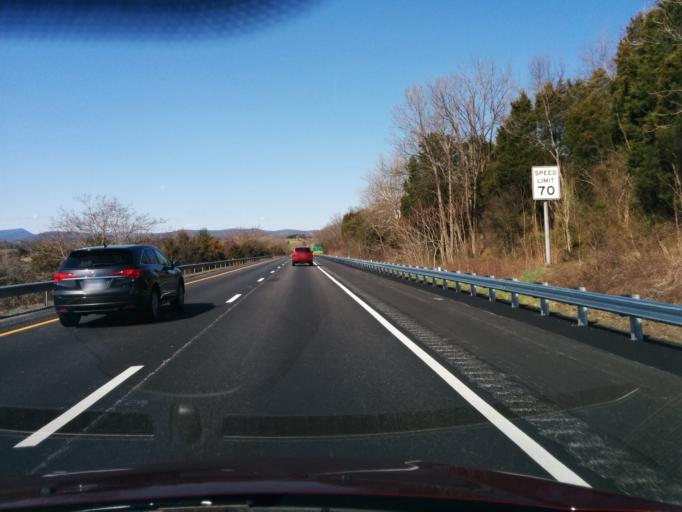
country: US
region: Virginia
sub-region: Rockbridge County
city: East Lexington
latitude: 37.7666
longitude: -79.4047
